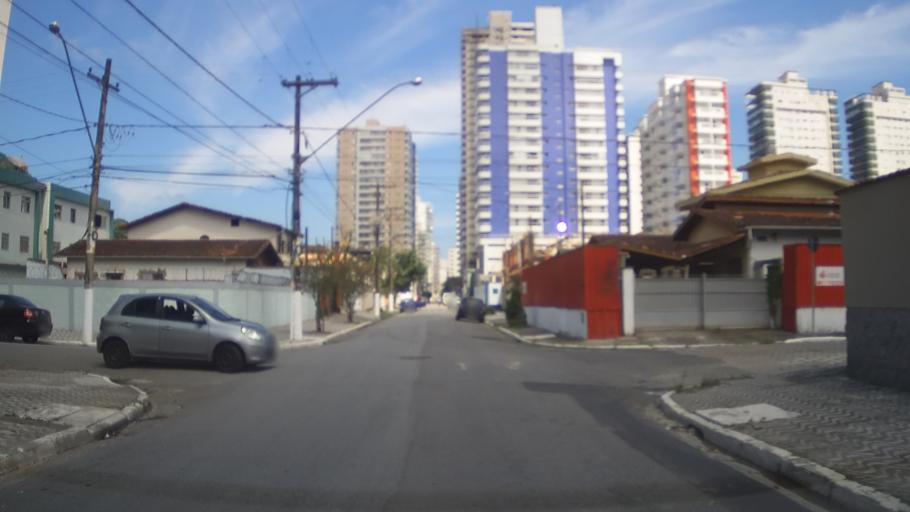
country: BR
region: Sao Paulo
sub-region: Praia Grande
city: Praia Grande
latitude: -24.0116
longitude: -46.3964
